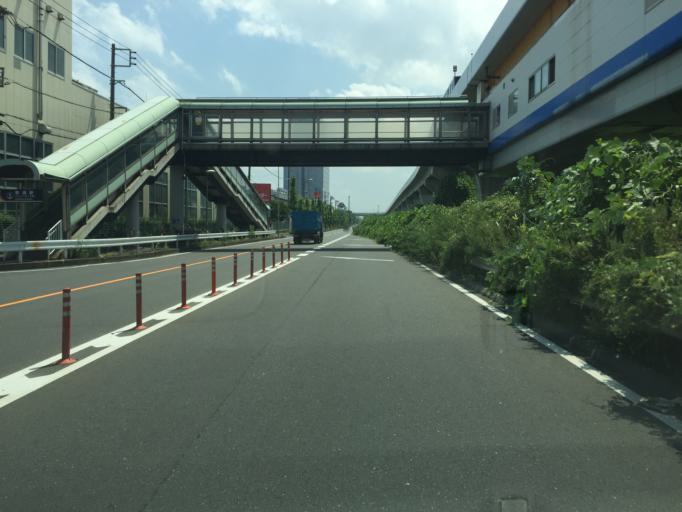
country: JP
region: Kanagawa
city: Yokosuka
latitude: 35.3585
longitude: 139.6438
